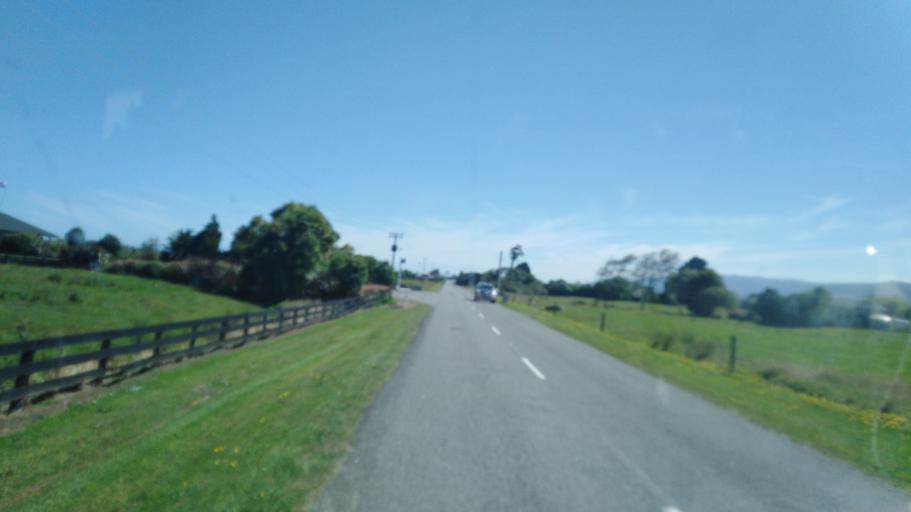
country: NZ
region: West Coast
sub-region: Buller District
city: Westport
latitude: -41.2579
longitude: 172.1317
